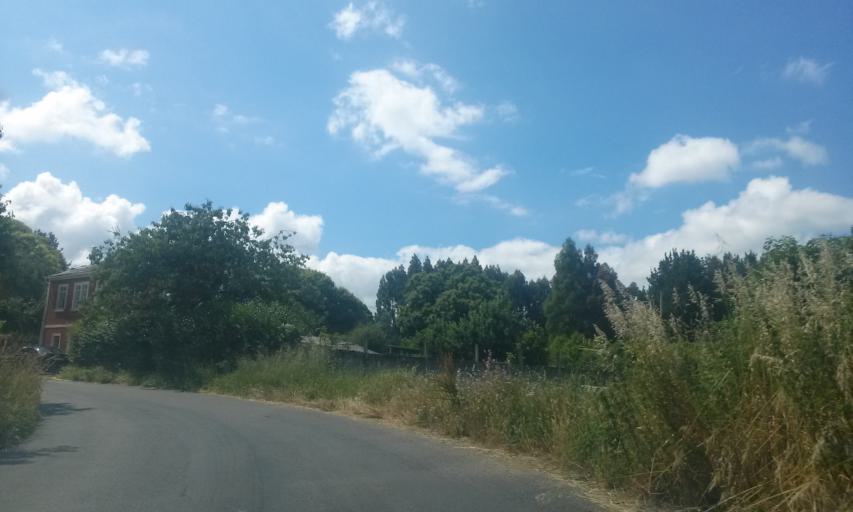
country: ES
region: Galicia
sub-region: Provincia de Lugo
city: Begonte
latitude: 43.1182
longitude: -7.6625
